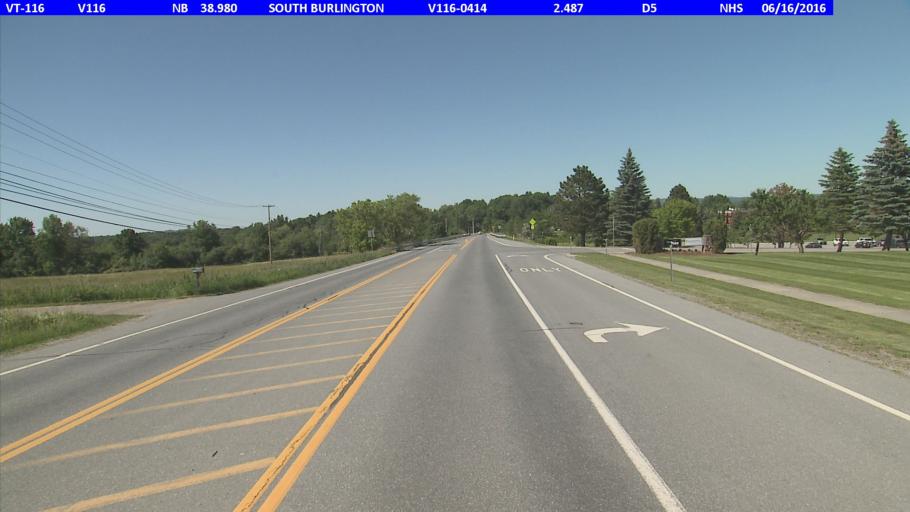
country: US
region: Vermont
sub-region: Chittenden County
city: South Burlington
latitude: 44.4456
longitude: -73.1583
